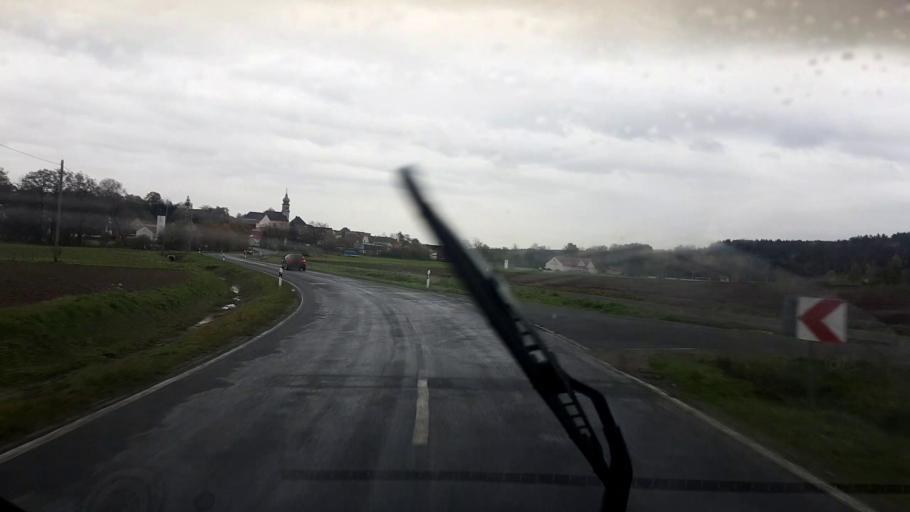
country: DE
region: Bavaria
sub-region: Upper Franconia
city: Burgwindheim
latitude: 49.8742
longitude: 10.6192
